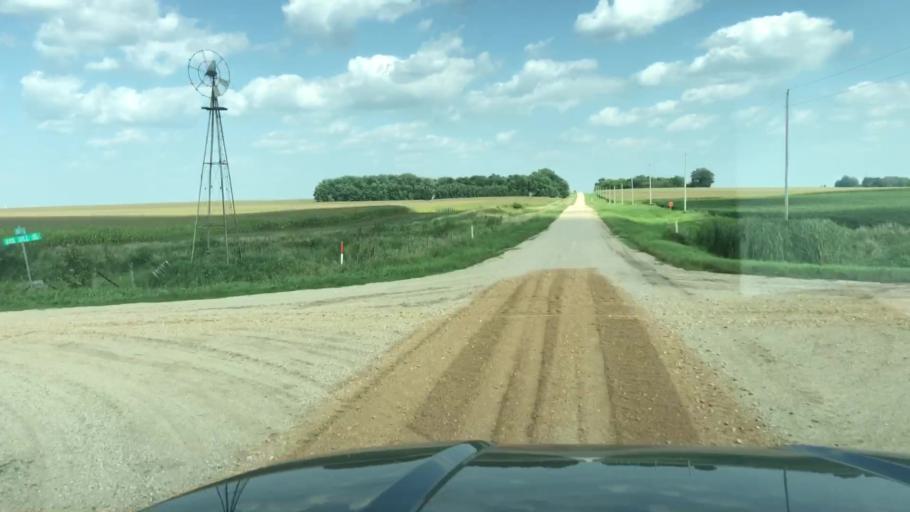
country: US
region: Iowa
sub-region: O'Brien County
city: Sheldon
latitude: 43.1568
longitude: -95.7824
